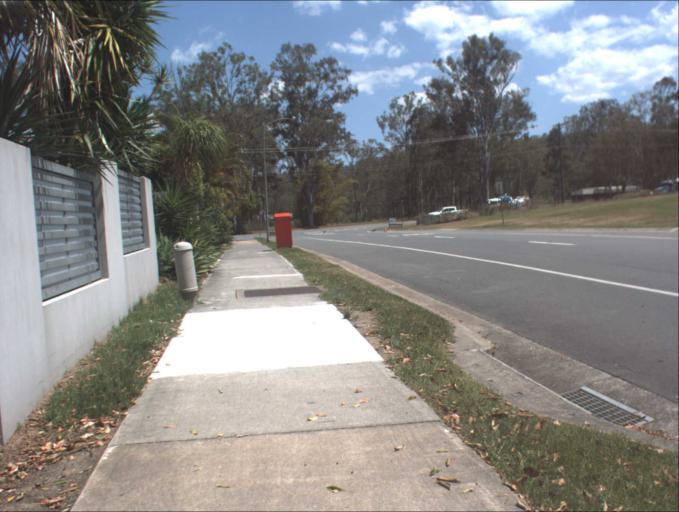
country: AU
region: Queensland
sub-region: Logan
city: Windaroo
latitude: -27.7524
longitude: 153.1887
